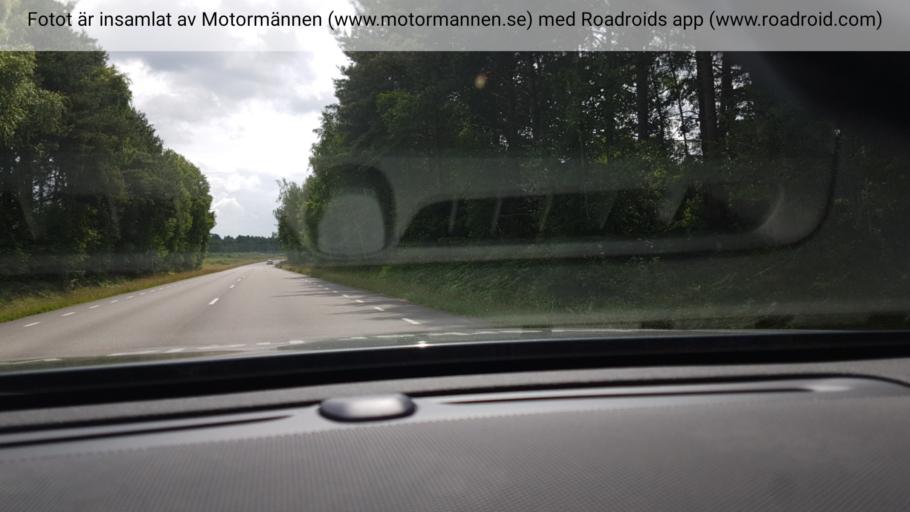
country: SE
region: Skane
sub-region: Hassleholms Kommun
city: Hassleholm
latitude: 56.1759
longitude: 13.7900
